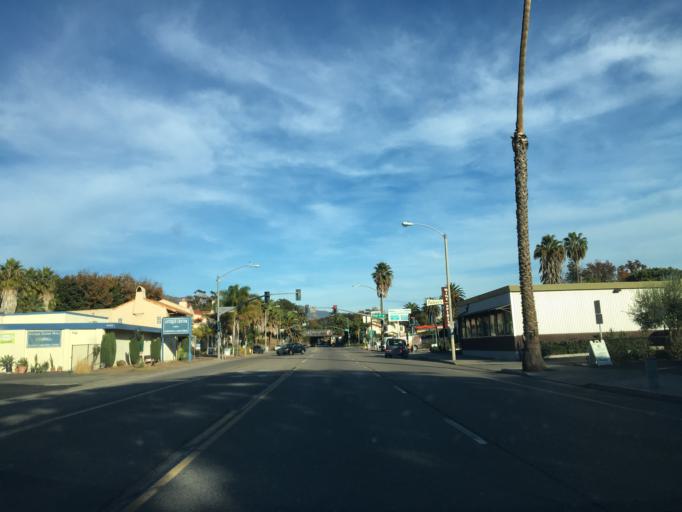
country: US
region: California
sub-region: Santa Barbara County
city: Goleta
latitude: 34.4398
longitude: -119.7720
